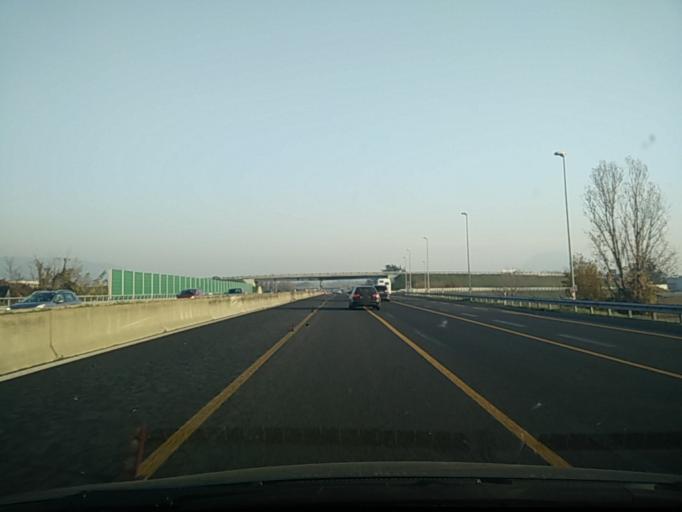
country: IT
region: Lombardy
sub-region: Provincia di Bergamo
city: Castelli Calepio
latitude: 45.6247
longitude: 9.8924
